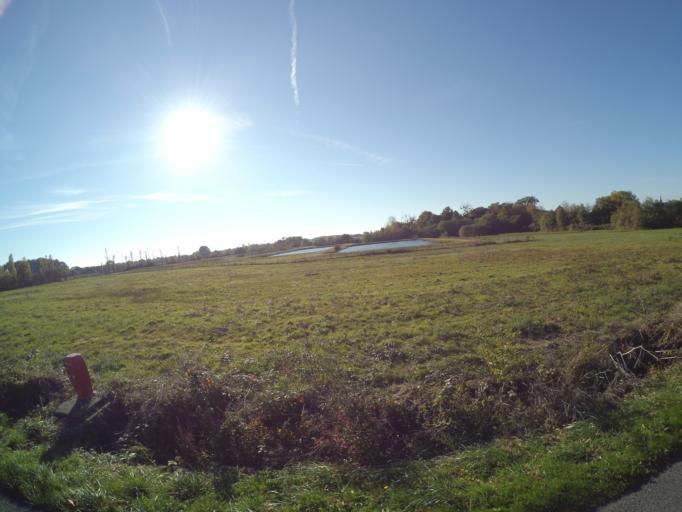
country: FR
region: Pays de la Loire
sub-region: Departement de la Loire-Atlantique
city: Saint-Lumine-de-Clisson
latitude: 47.0807
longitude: -1.3315
